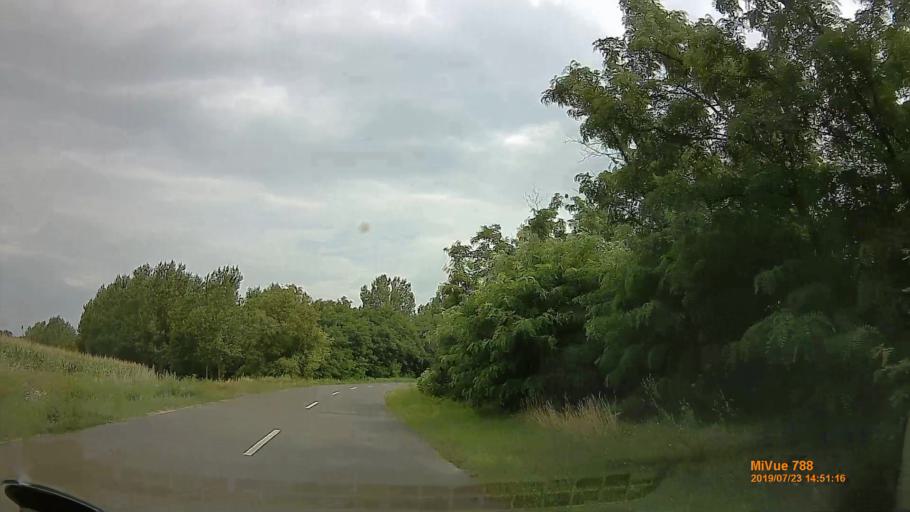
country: HU
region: Szabolcs-Szatmar-Bereg
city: Kalmanhaza
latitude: 47.8841
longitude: 21.6515
